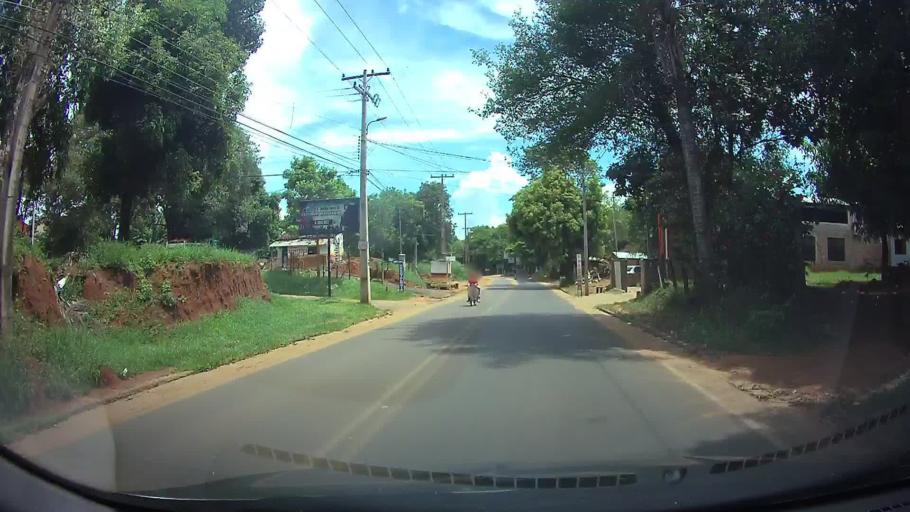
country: PY
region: Central
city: San Lorenzo
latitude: -25.3037
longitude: -57.4911
